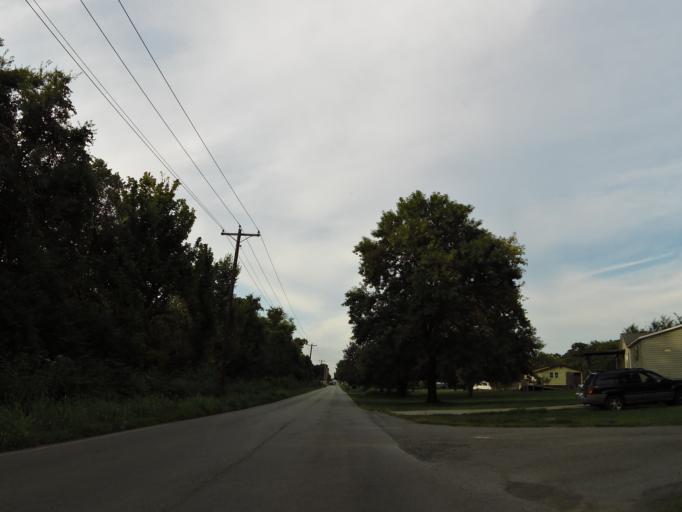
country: US
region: Tennessee
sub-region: Blount County
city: Alcoa
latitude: 35.8110
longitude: -83.9613
